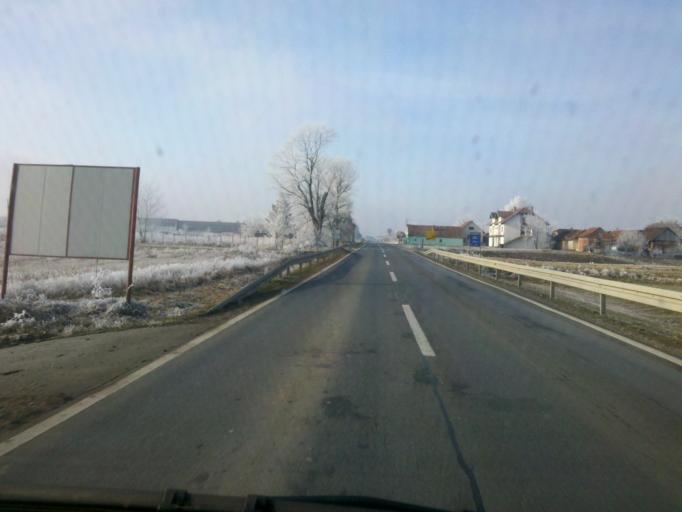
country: HR
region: Virovitick-Podravska
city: Pitomaca
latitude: 45.9650
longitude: 17.2110
